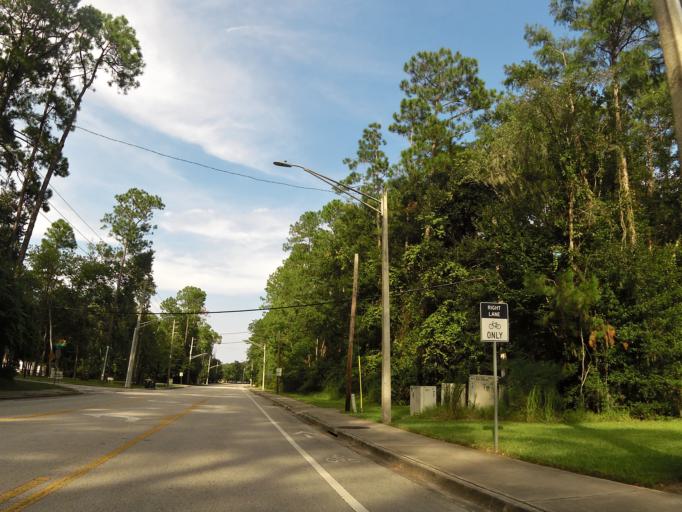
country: US
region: Florida
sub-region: Saint Johns County
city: Fruit Cove
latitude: 30.1887
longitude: -81.5914
